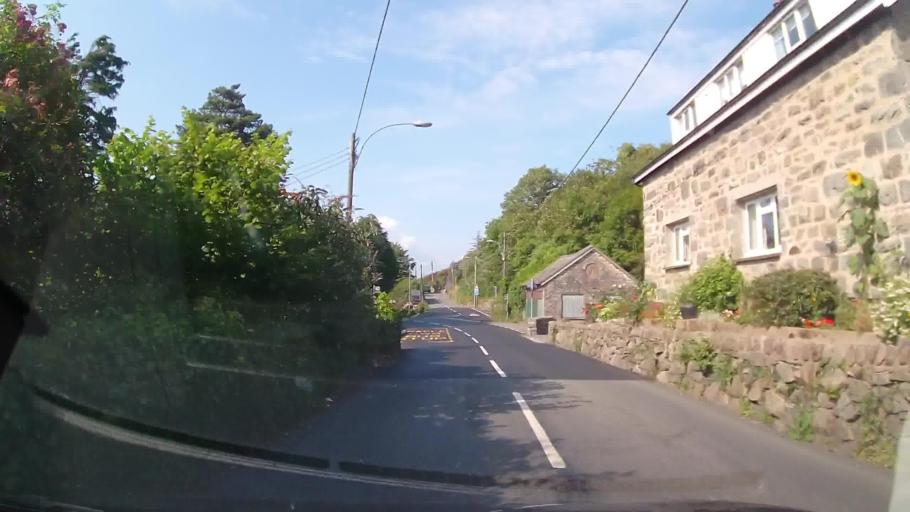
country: GB
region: Wales
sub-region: Gwynedd
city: Llanfair
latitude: 52.8520
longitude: -4.1134
